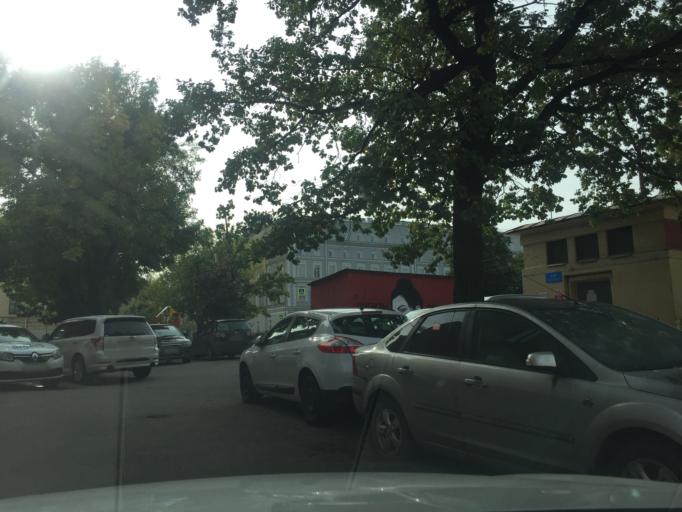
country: RU
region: St.-Petersburg
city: Centralniy
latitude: 59.9338
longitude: 30.3655
